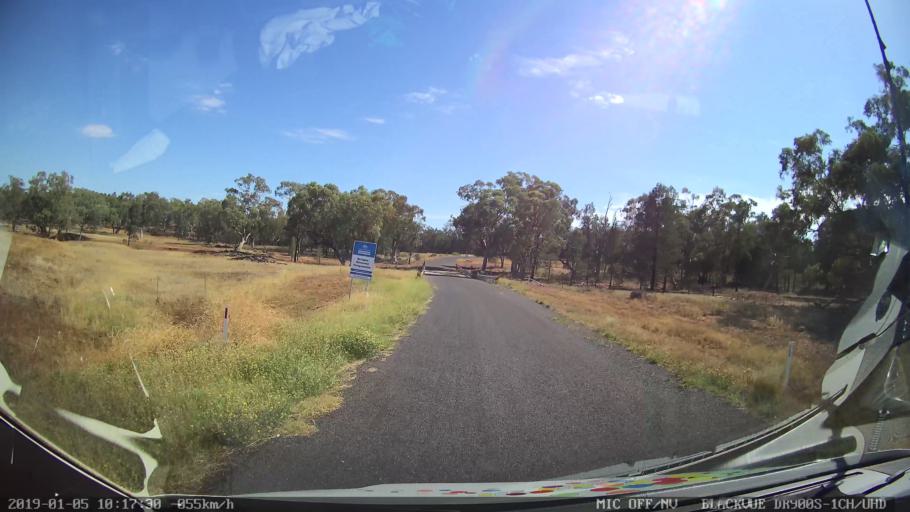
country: AU
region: New South Wales
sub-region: Gilgandra
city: Gilgandra
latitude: -31.5665
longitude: 148.9607
